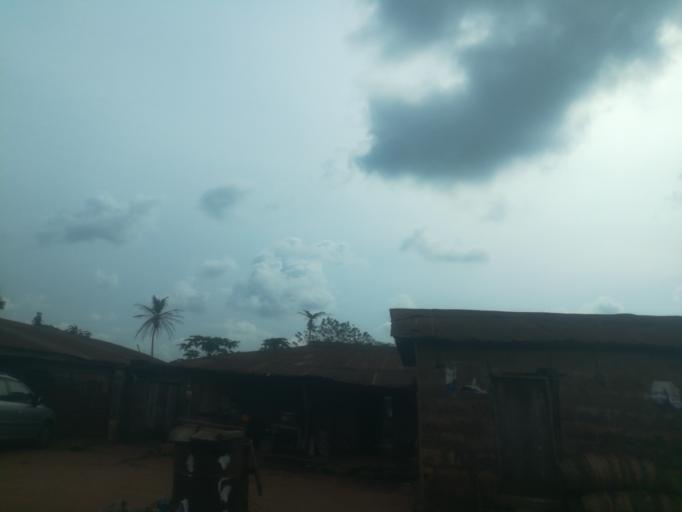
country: NG
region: Ogun
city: Ayetoro
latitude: 7.3912
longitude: 3.0155
